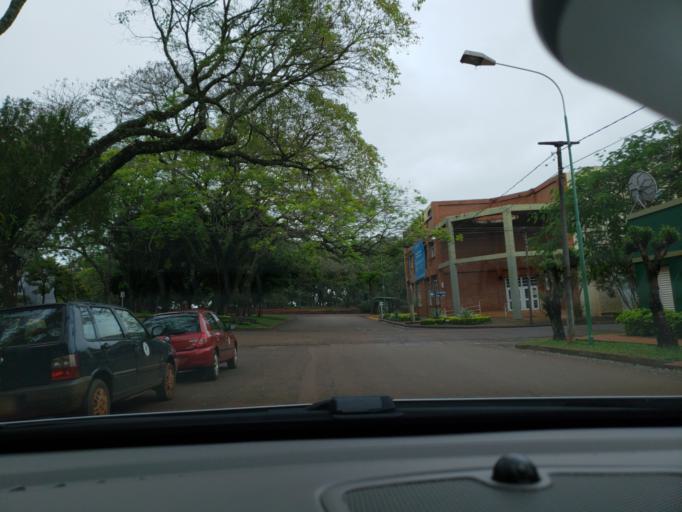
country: AR
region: Misiones
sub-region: Departamento de Apostoles
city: Apostoles
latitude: -27.9129
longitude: -55.7538
